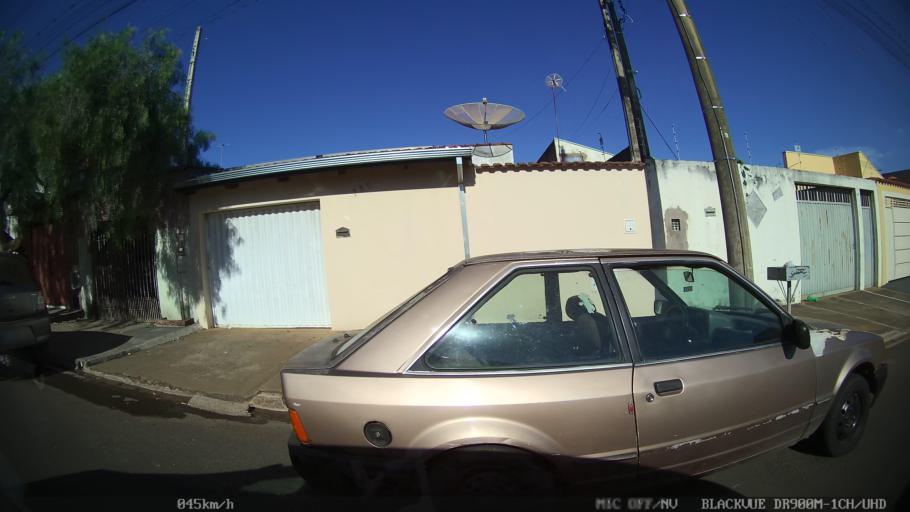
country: BR
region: Sao Paulo
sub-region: Franca
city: Franca
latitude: -20.4797
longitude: -47.4191
